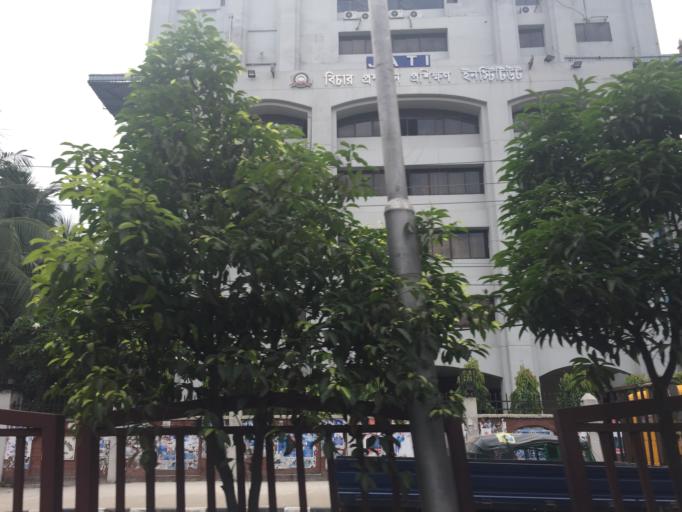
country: BD
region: Dhaka
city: Paltan
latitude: 23.7267
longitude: 90.4043
